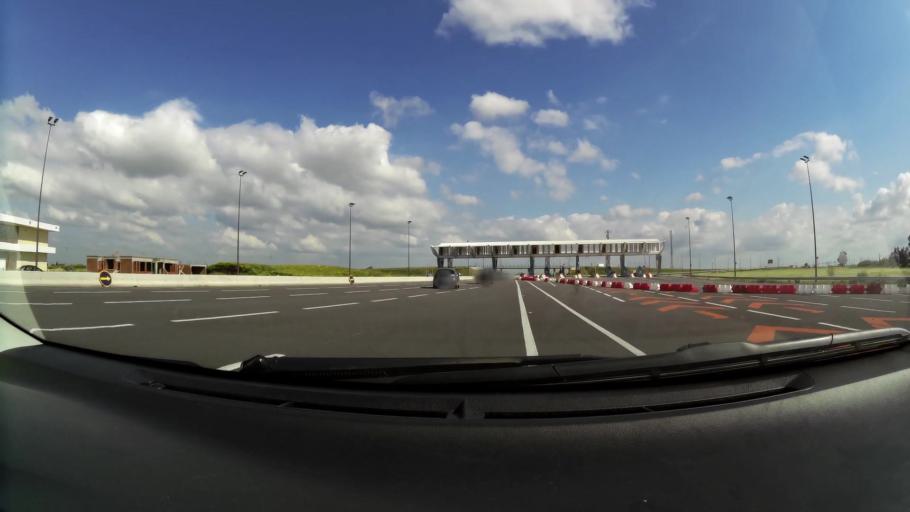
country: MA
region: Chaouia-Ouardigha
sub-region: Settat Province
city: Berrechid
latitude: 33.3195
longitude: -7.6035
